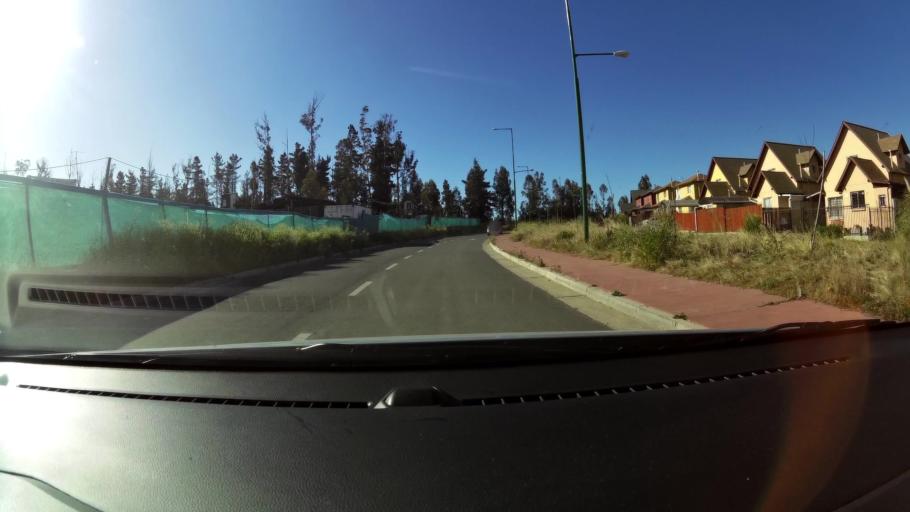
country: CL
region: Valparaiso
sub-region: Provincia de Valparaiso
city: Valparaiso
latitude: -33.1223
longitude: -71.5855
